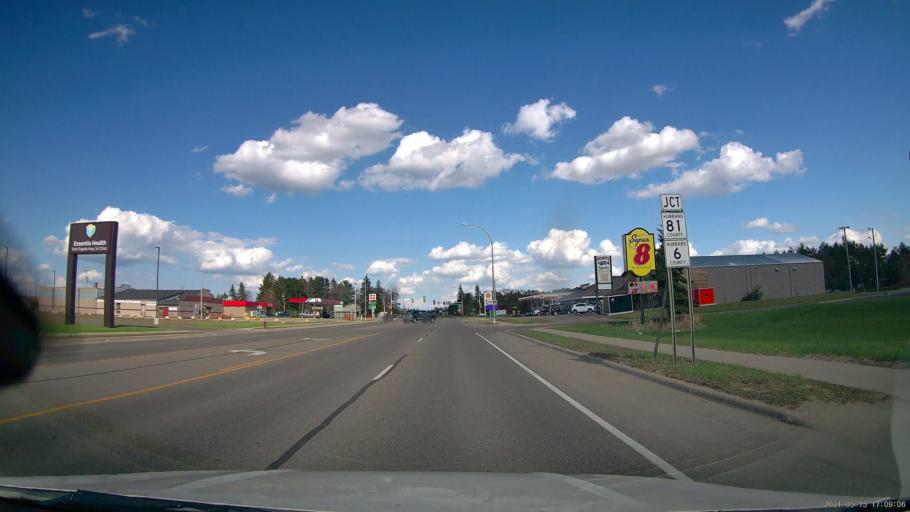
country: US
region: Minnesota
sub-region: Hubbard County
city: Park Rapids
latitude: 46.9218
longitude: -95.0393
